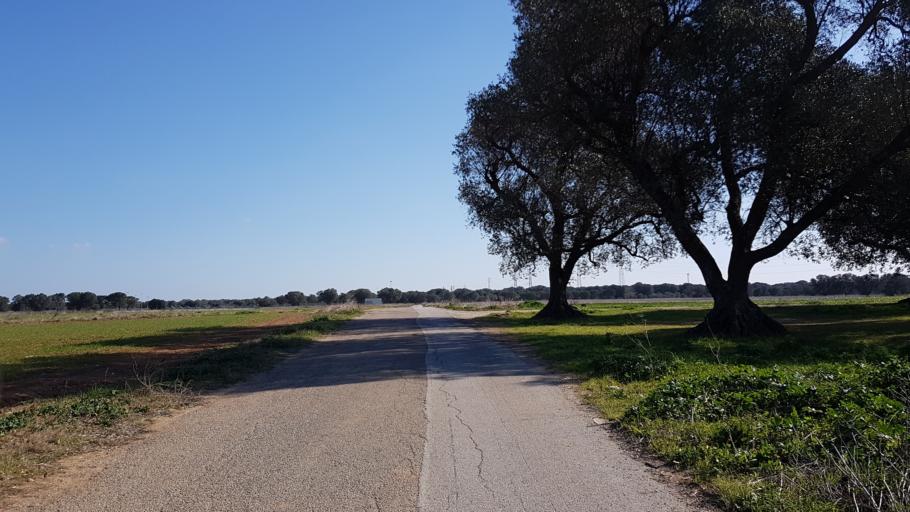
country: IT
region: Apulia
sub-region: Provincia di Brindisi
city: Mesagne
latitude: 40.6204
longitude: 17.8299
